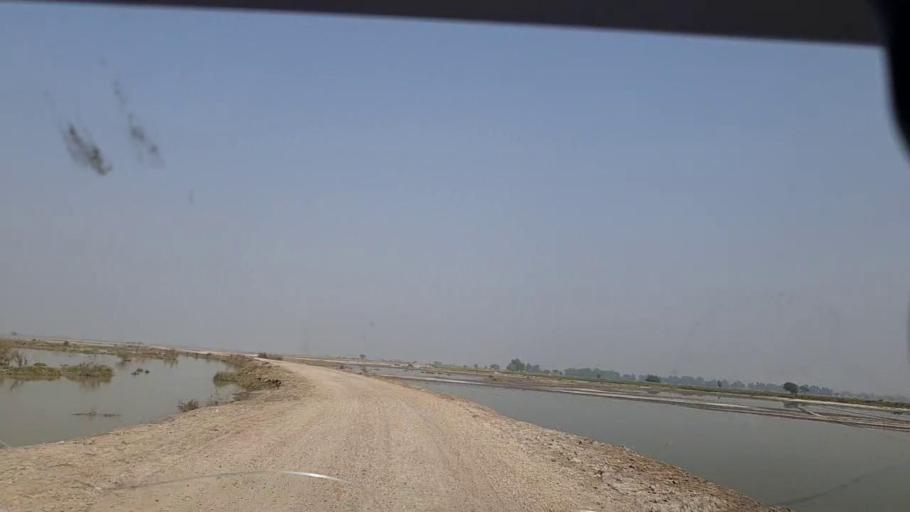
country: PK
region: Sindh
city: Shikarpur
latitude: 28.0422
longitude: 68.6506
